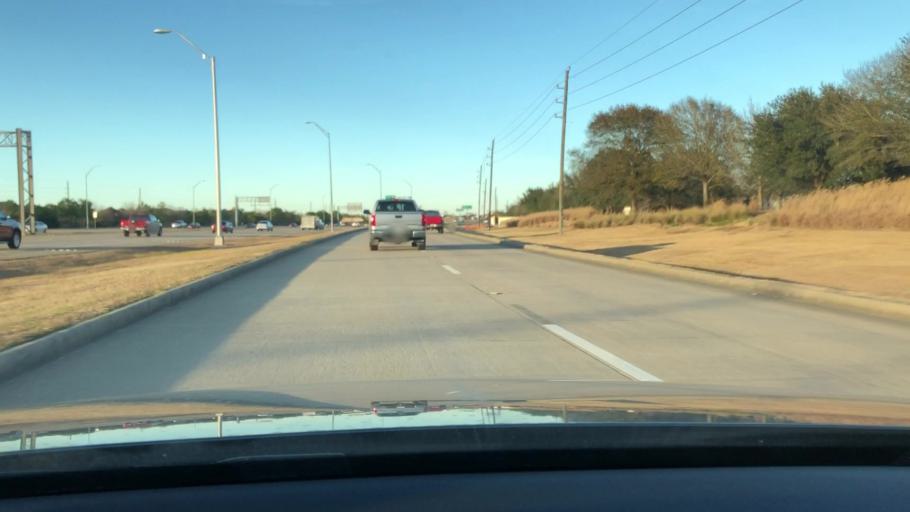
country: US
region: Texas
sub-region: Fort Bend County
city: Cinco Ranch
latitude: 29.7071
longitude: -95.7757
